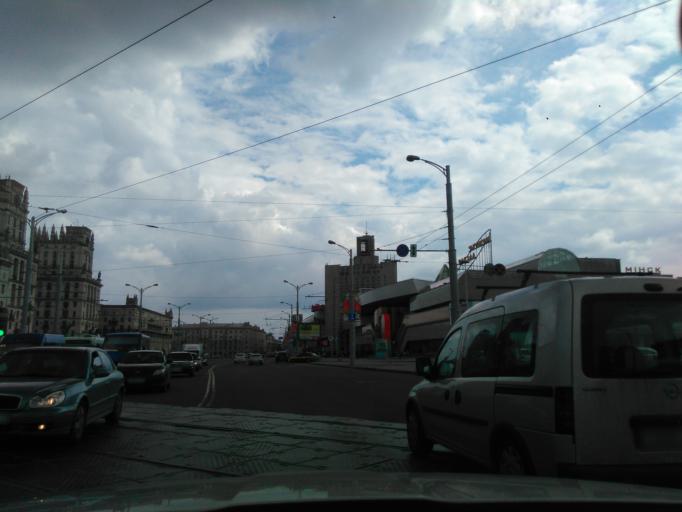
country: BY
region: Minsk
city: Minsk
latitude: 53.8919
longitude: 27.5483
